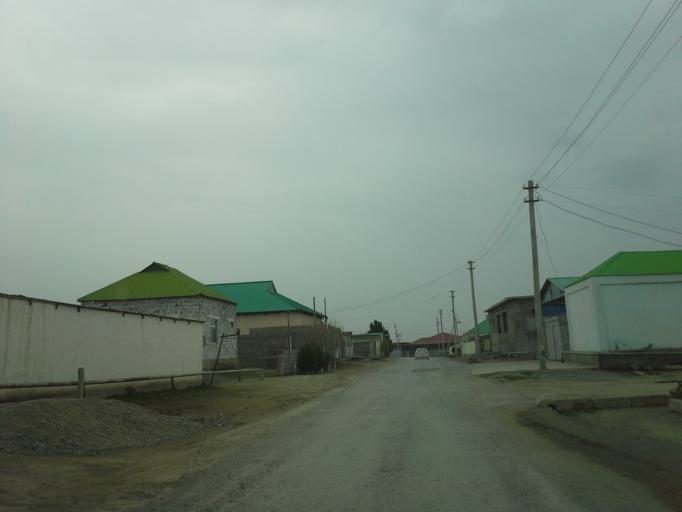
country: TM
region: Ahal
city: Abadan
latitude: 37.9751
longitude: 58.2273
